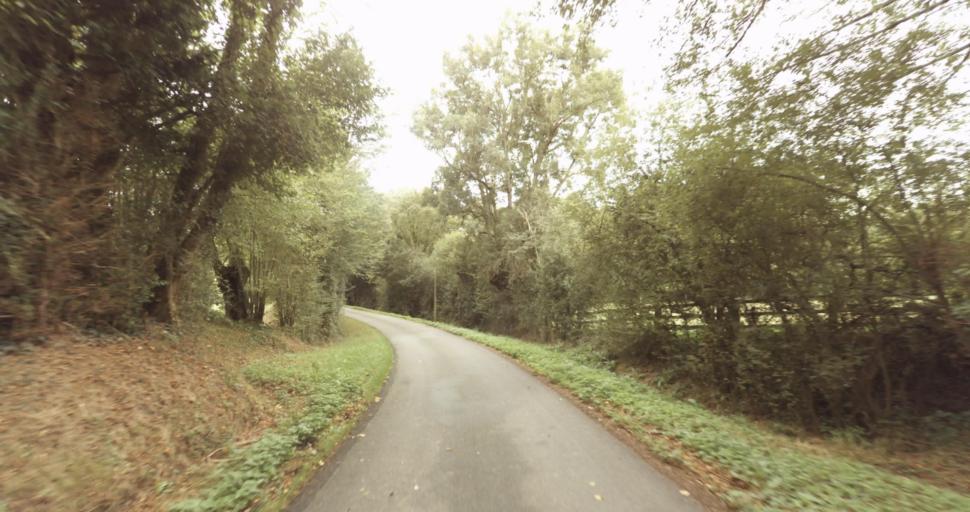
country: FR
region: Lower Normandy
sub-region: Departement de l'Orne
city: Gace
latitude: 48.7515
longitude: 0.3156
